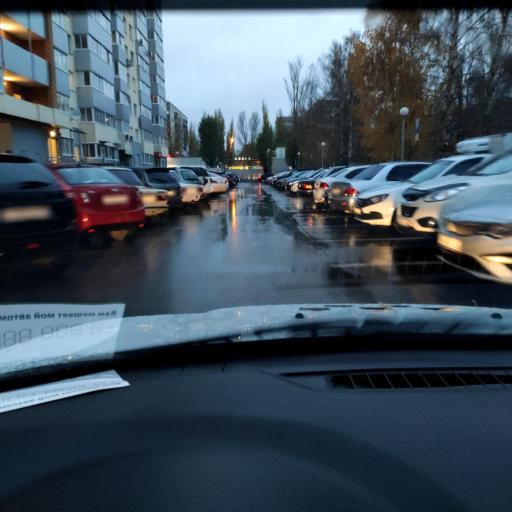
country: RU
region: Samara
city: Tol'yatti
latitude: 53.5077
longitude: 49.4254
